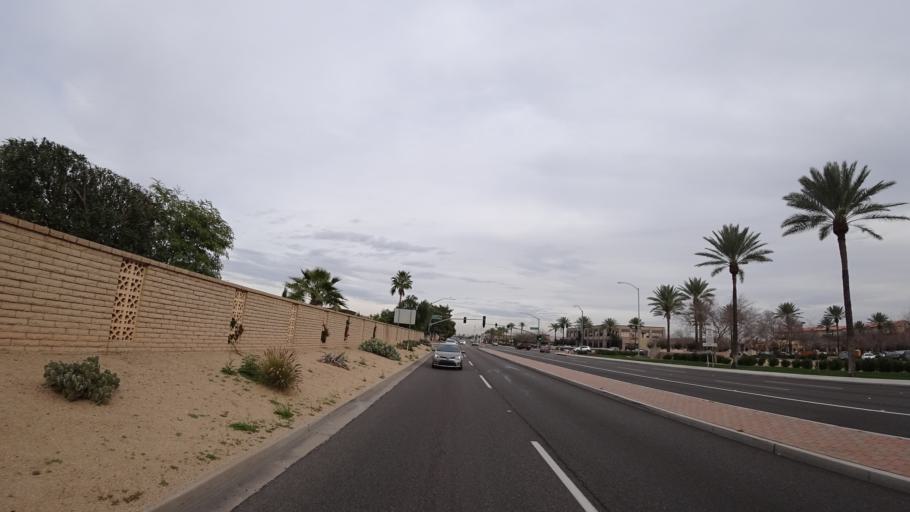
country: US
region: Arizona
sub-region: Maricopa County
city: Sun City
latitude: 33.6097
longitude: -112.2585
